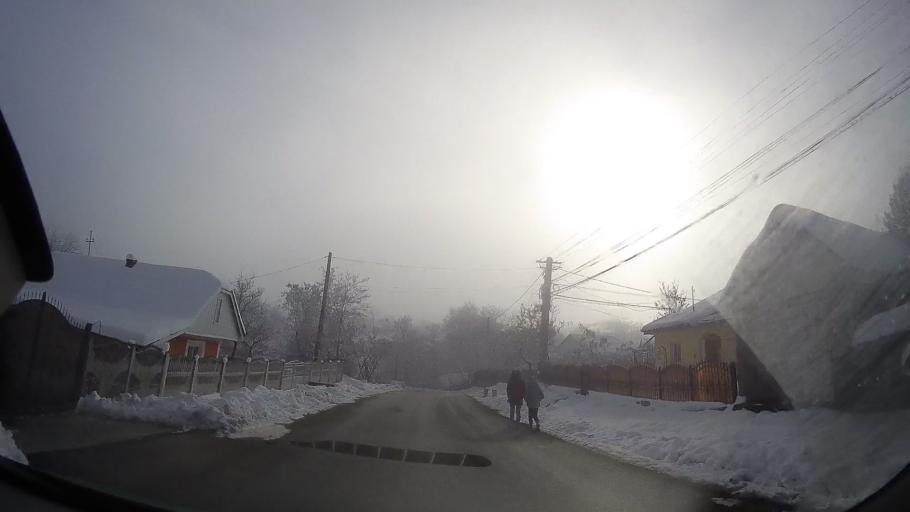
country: RO
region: Iasi
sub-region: Comuna Valea Seaca
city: Topile
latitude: 47.2474
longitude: 26.6604
